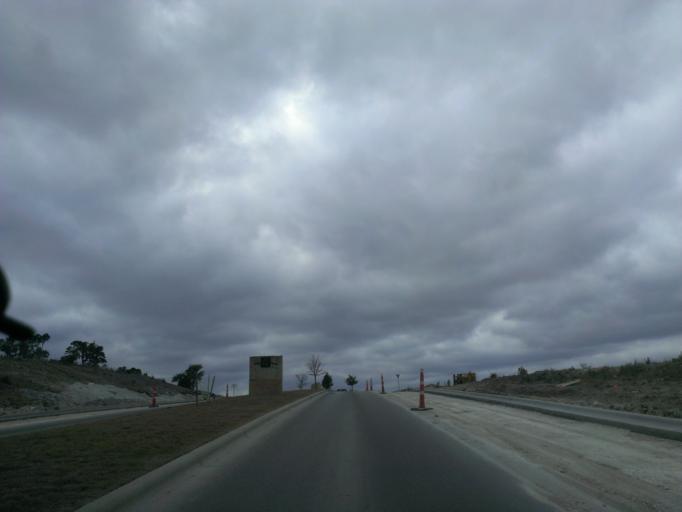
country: US
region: Texas
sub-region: Travis County
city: The Hills
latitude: 30.3453
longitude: -98.0246
